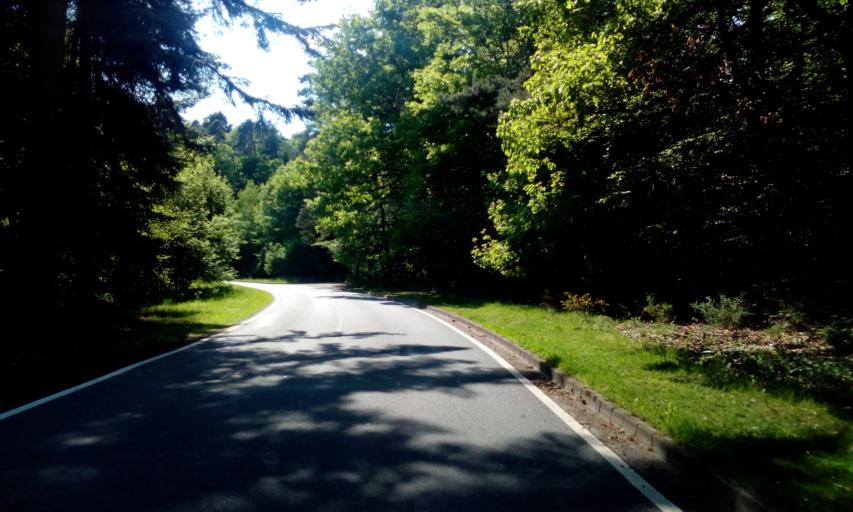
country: DE
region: Rheinland-Pfalz
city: Leiwen
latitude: 49.8075
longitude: 6.8954
